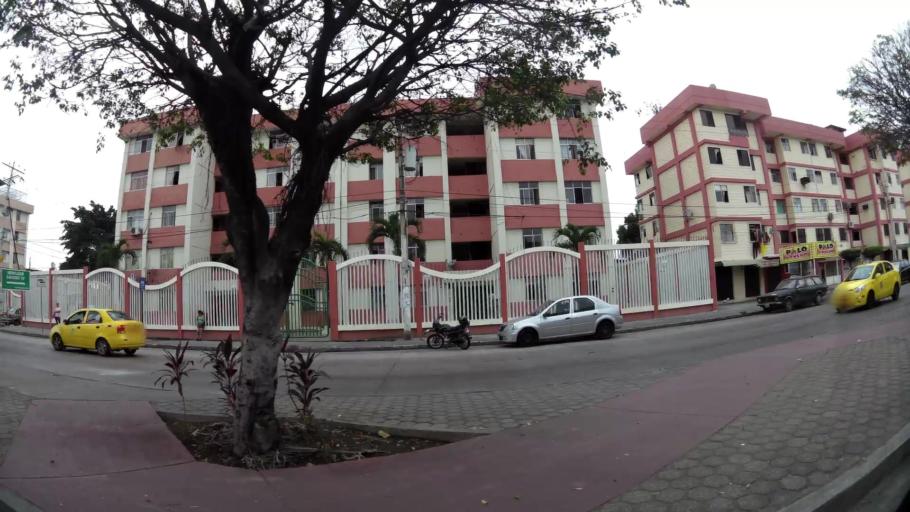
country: EC
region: Guayas
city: Eloy Alfaro
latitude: -2.1273
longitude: -79.8875
